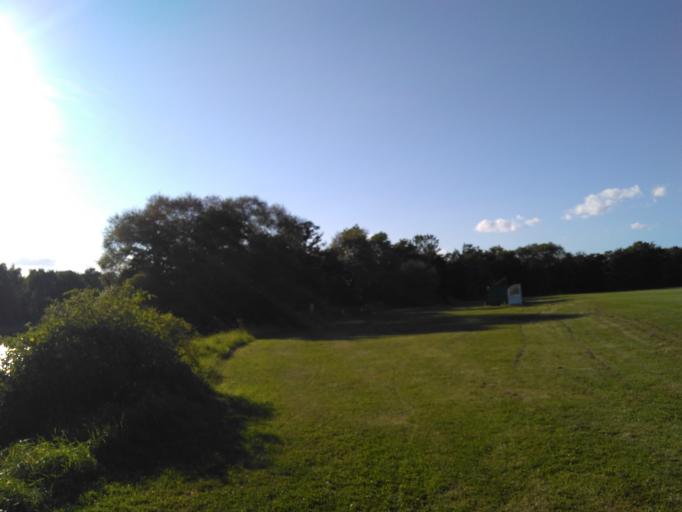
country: SE
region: OEstergoetland
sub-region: Norrkopings Kommun
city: Norrkoping
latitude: 58.5938
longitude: 16.1412
